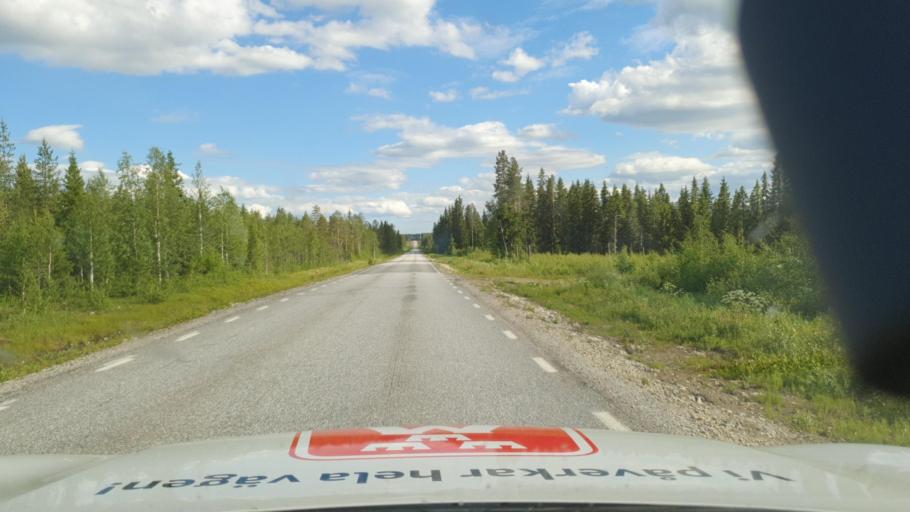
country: SE
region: Vaesterbotten
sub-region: Skelleftea Kommun
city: Langsele
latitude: 64.7169
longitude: 19.9789
